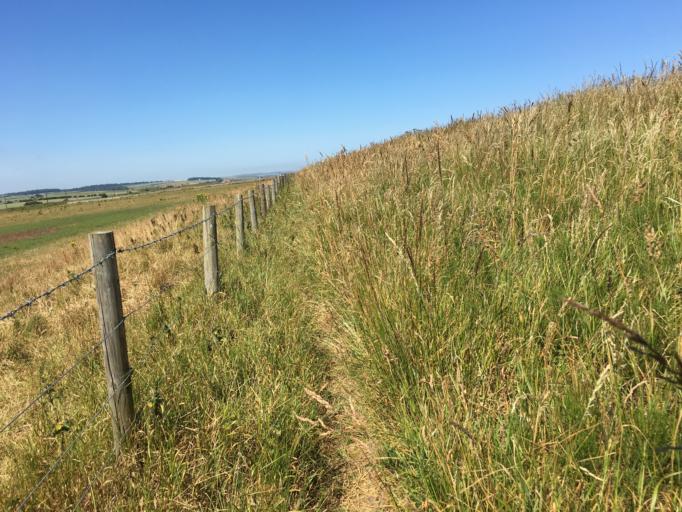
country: GB
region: England
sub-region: Northumberland
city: Ancroft
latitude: 55.7103
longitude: -1.9310
